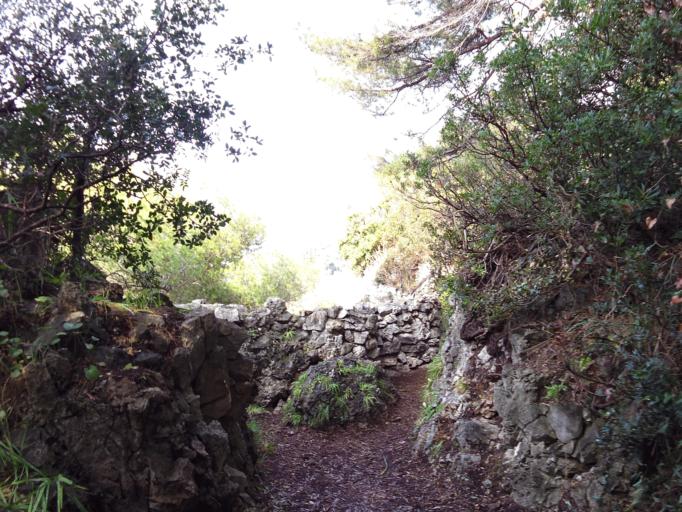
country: FR
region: Provence-Alpes-Cote d'Azur
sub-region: Departement des Alpes-Maritimes
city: Antibes
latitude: 43.5445
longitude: 7.1296
